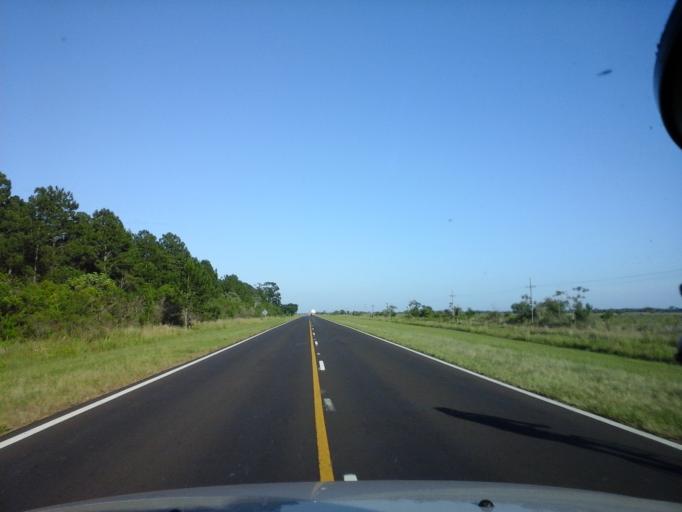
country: AR
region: Corrientes
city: Ita Ibate
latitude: -27.5113
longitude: -57.2368
